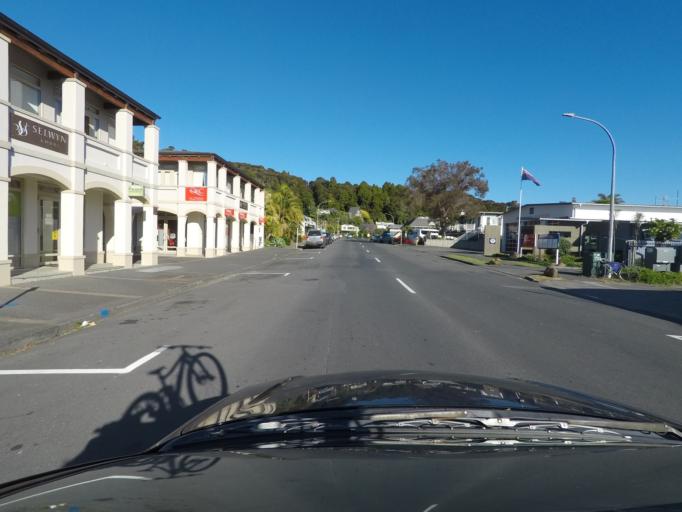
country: NZ
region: Northland
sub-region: Far North District
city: Paihia
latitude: -35.2818
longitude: 174.0906
